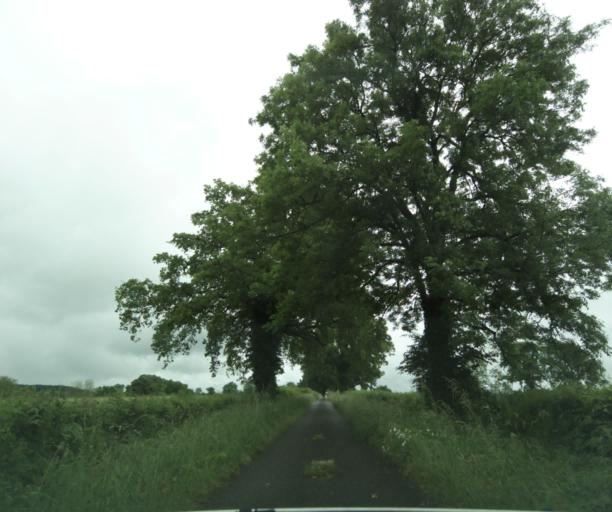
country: FR
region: Bourgogne
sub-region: Departement de Saone-et-Loire
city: Charolles
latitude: 46.4577
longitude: 4.3631
